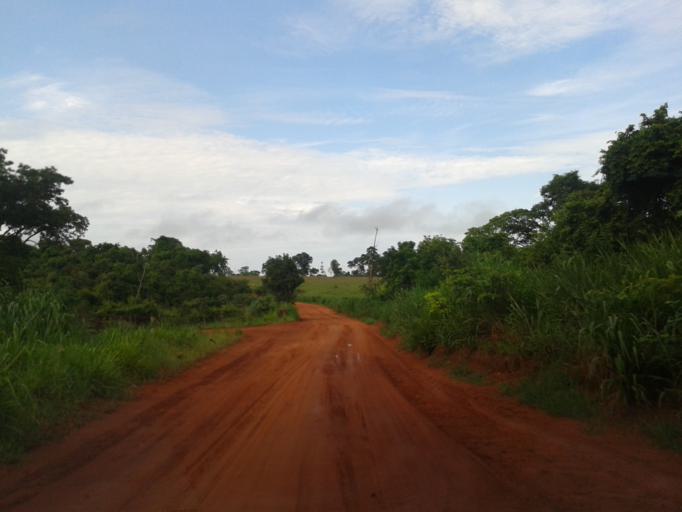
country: BR
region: Minas Gerais
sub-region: Santa Vitoria
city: Santa Vitoria
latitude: -19.1307
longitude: -50.5513
